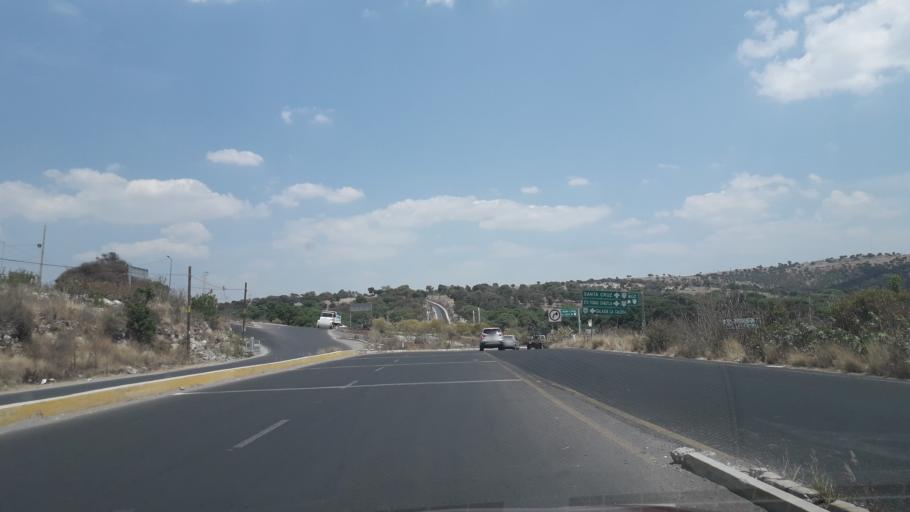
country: MX
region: Puebla
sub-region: Puebla
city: Galaxia la Calera
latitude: 18.9909
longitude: -98.1632
